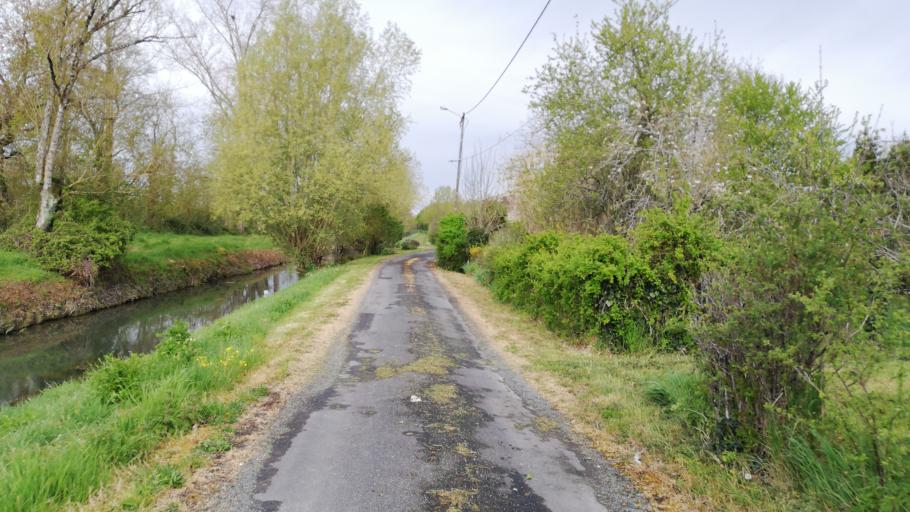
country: FR
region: Pays de la Loire
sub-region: Departement de la Vendee
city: Maillezais
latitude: 46.3301
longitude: -0.7224
